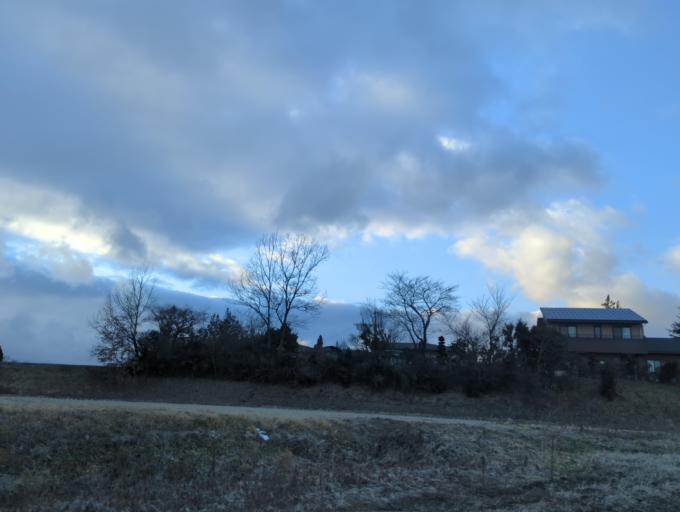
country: JP
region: Fukushima
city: Koriyama
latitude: 37.4511
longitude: 140.4023
